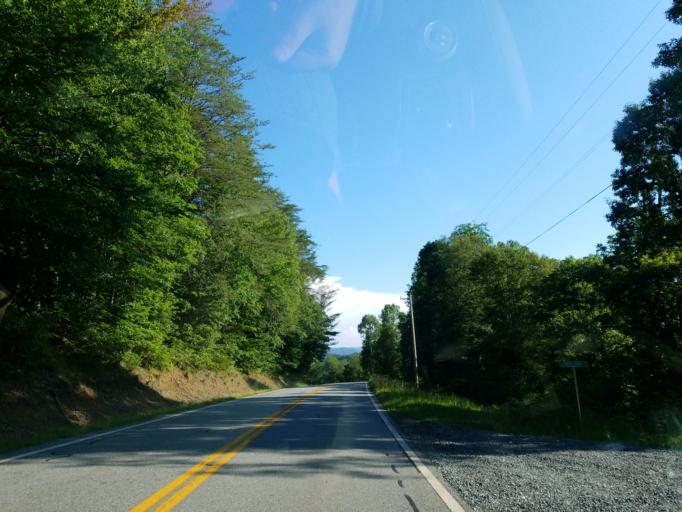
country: US
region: Georgia
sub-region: Fannin County
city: Blue Ridge
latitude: 34.7823
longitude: -84.1849
